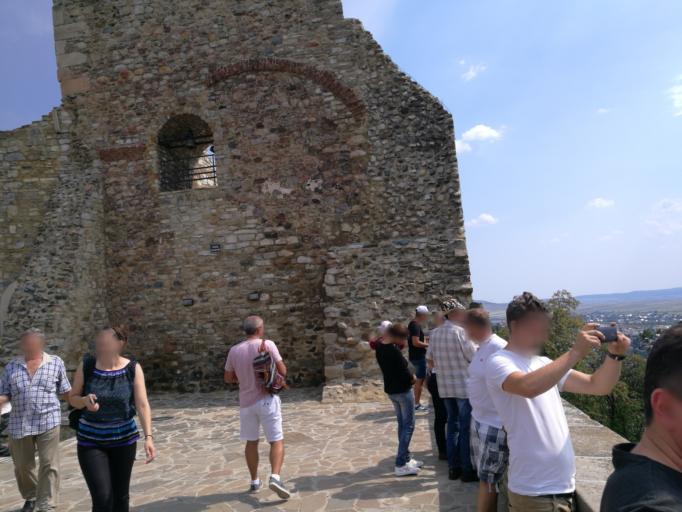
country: RO
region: Neamt
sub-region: Oras Targu Neamt
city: Humulesti
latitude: 47.2142
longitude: 26.3433
